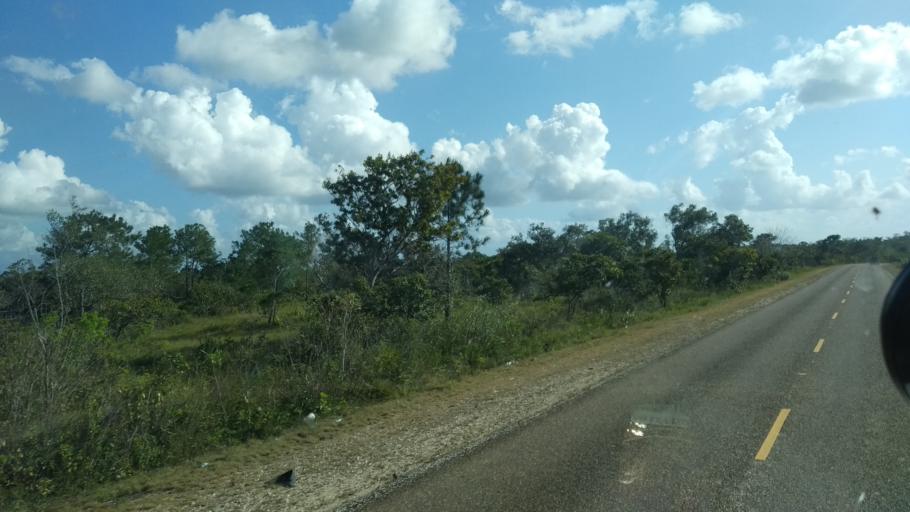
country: BZ
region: Cayo
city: Belmopan
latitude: 17.3840
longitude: -88.5187
